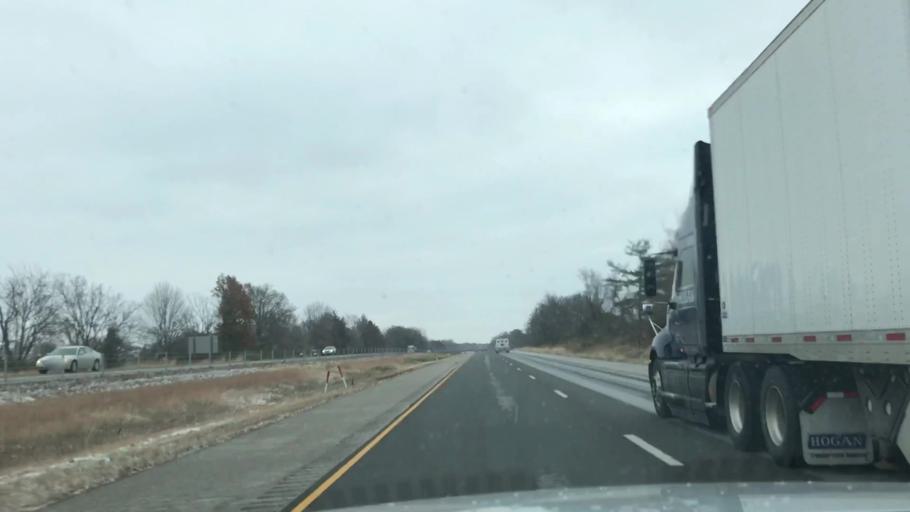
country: US
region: Illinois
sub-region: Madison County
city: Glen Carbon
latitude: 38.7567
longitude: -89.9912
